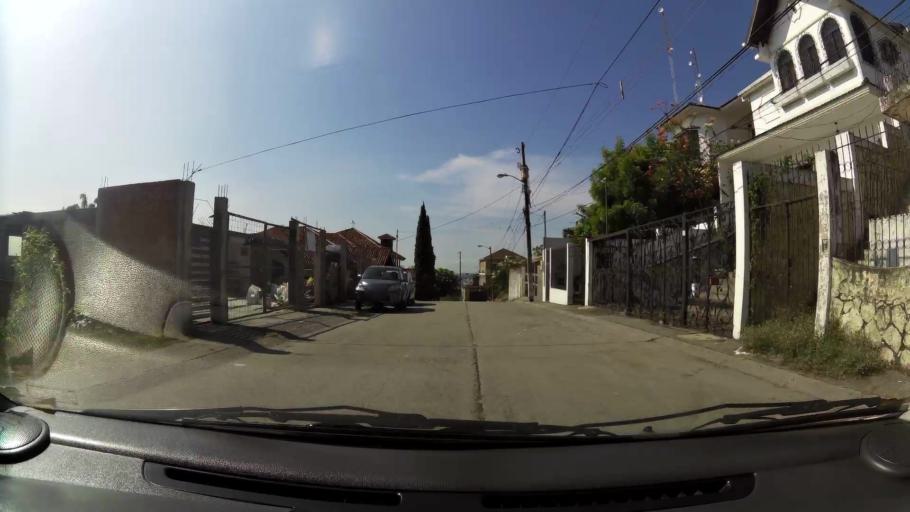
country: EC
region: Guayas
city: Guayaquil
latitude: -2.1820
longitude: -79.9143
